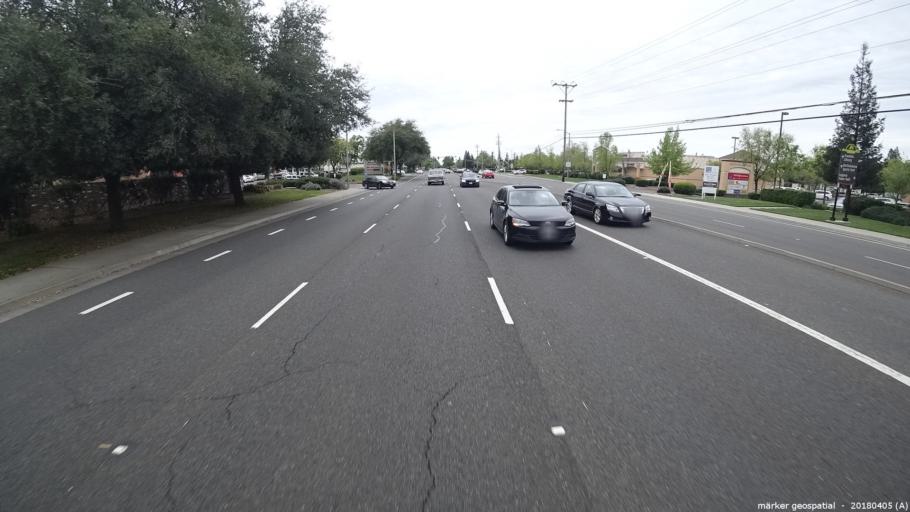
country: US
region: California
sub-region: Sacramento County
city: Laguna
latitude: 38.4248
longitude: -121.4477
